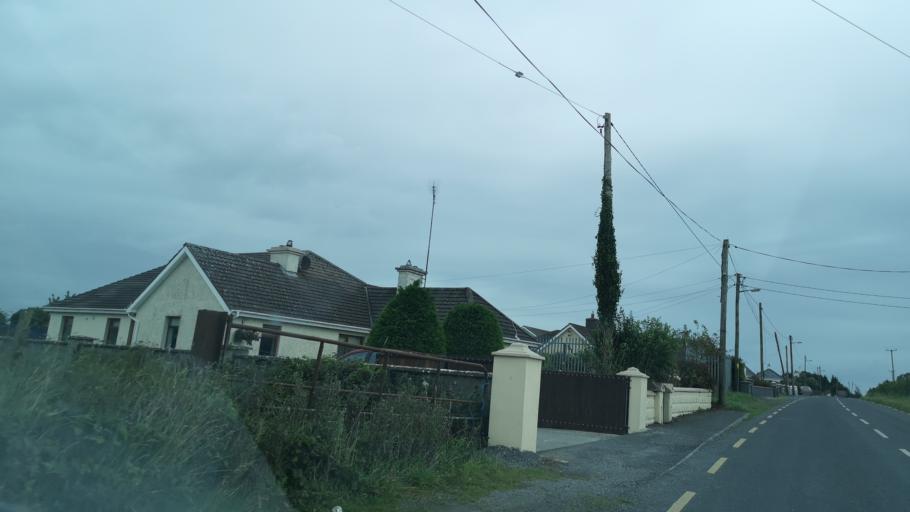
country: IE
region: Leinster
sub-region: Uibh Fhaili
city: Banagher
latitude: 53.1976
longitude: -7.9704
